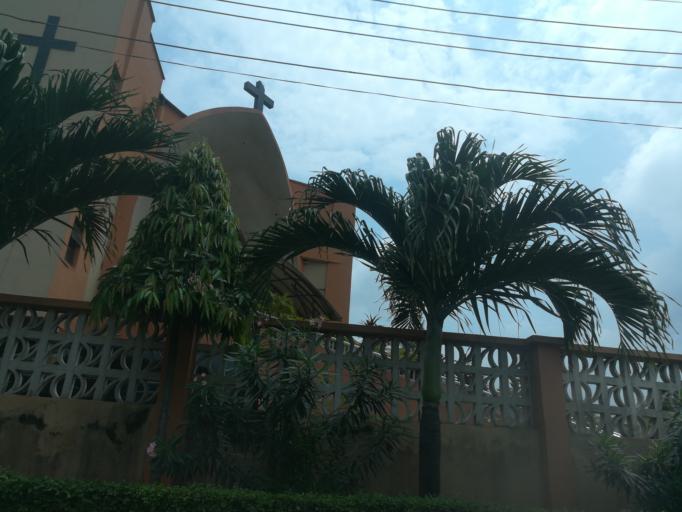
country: NG
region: Lagos
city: Ojota
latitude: 6.5884
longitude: 3.3634
